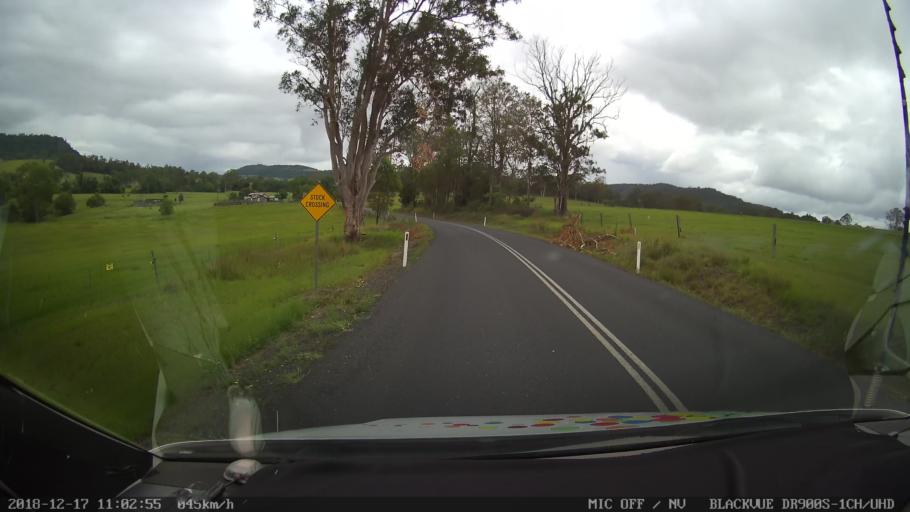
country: AU
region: New South Wales
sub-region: Kyogle
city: Kyogle
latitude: -28.8097
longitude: 152.6349
